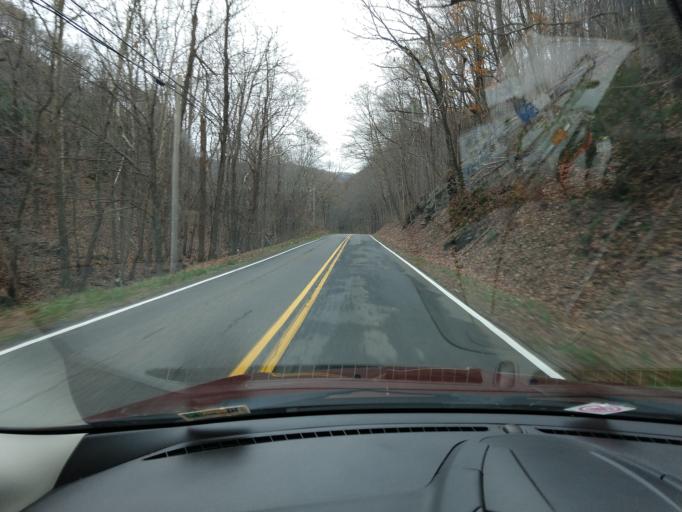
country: US
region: West Virginia
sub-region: Greenbrier County
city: White Sulphur Springs
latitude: 37.7451
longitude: -80.2369
